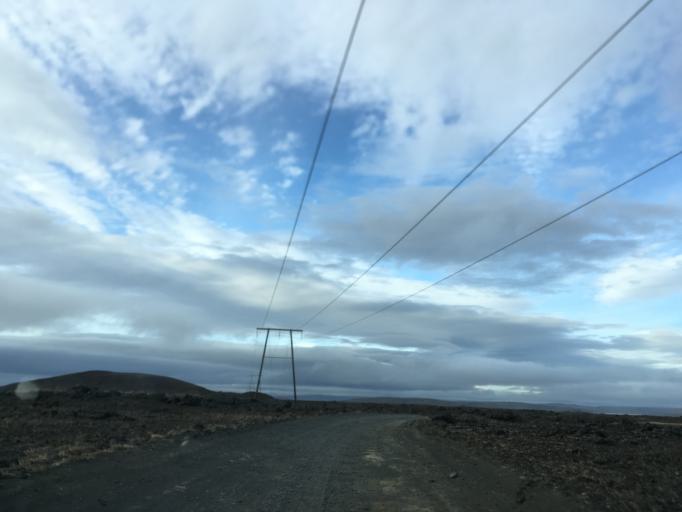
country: IS
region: South
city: Vestmannaeyjar
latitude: 64.1194
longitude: -19.1161
